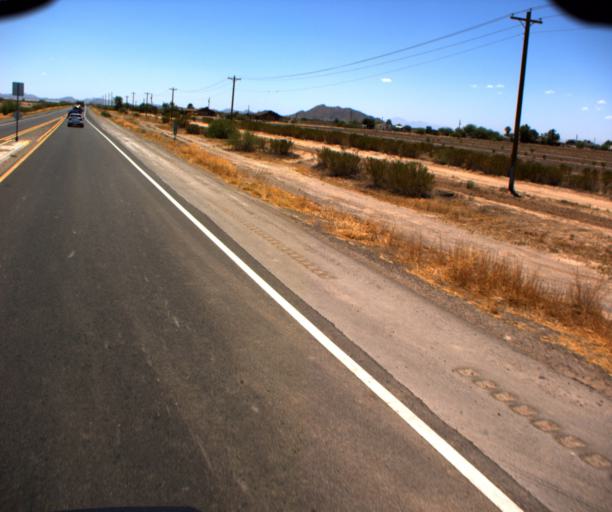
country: US
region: Arizona
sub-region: Maricopa County
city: Sun Lakes
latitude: 33.2009
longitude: -111.8410
